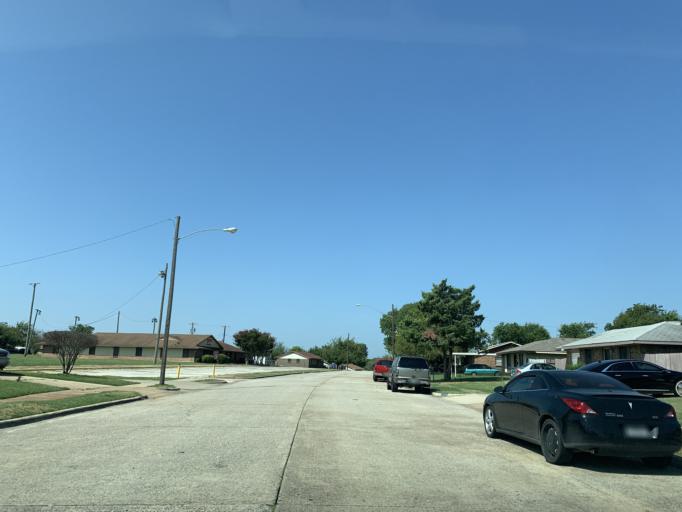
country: US
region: Texas
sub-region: Dallas County
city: Hutchins
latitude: 32.6681
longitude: -96.7456
